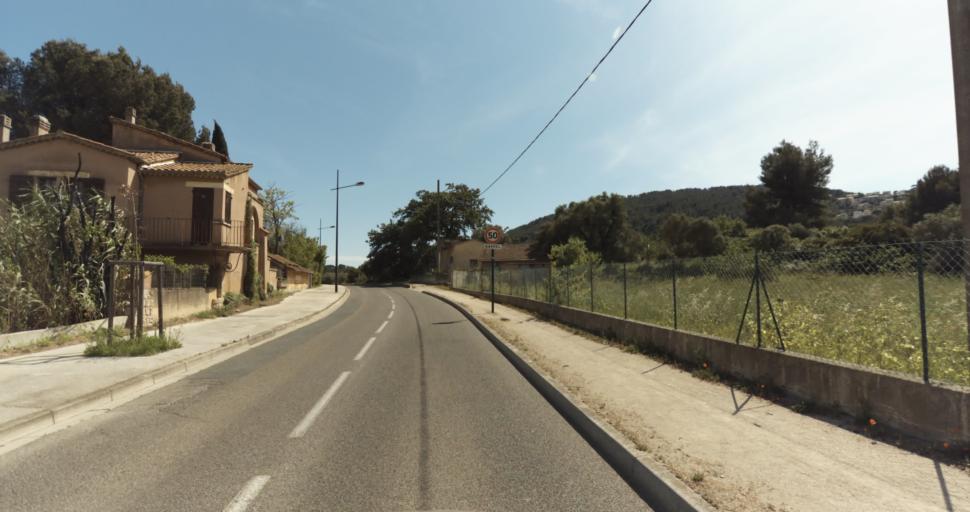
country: FR
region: Provence-Alpes-Cote d'Azur
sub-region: Departement du Var
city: Hyeres
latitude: 43.1019
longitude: 6.1211
